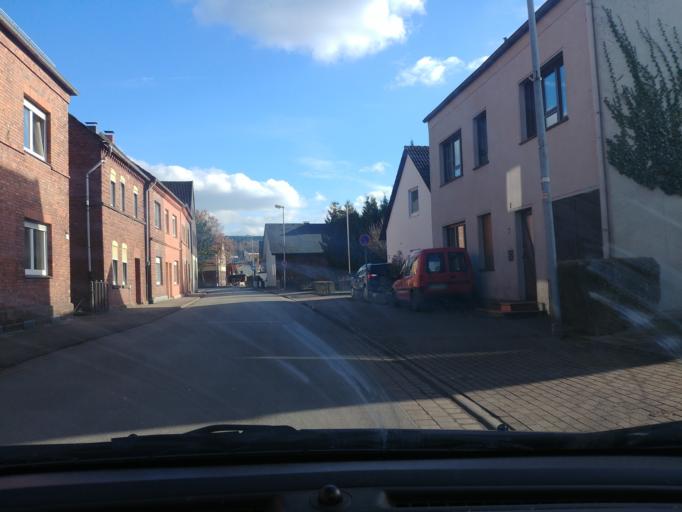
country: DE
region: Lower Saxony
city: Holzminden
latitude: 51.7960
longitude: 9.4257
